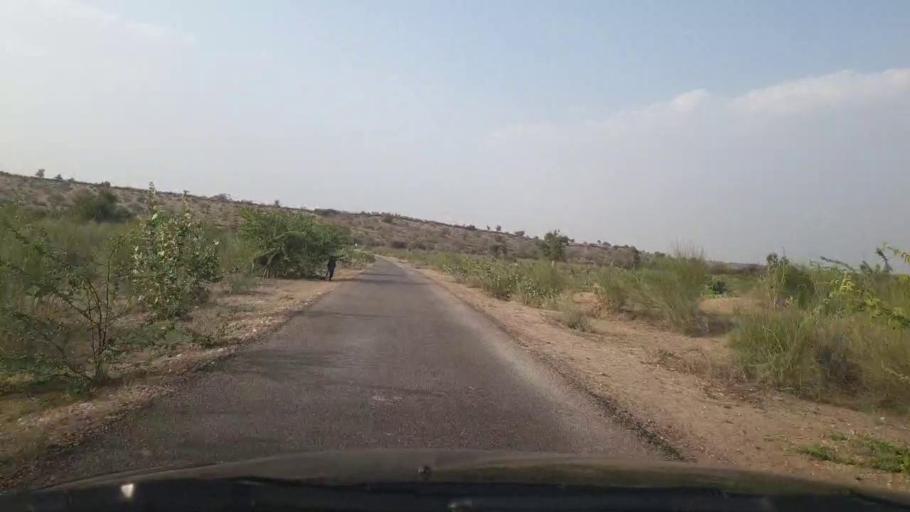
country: PK
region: Sindh
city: Islamkot
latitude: 25.0719
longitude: 70.5657
